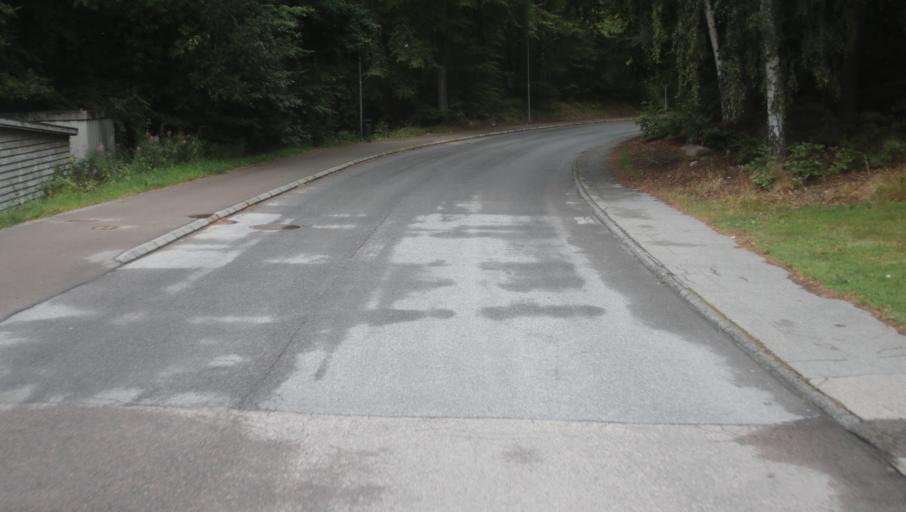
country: SE
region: Blekinge
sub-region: Karlshamns Kommun
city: Svangsta
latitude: 56.2601
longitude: 14.7758
